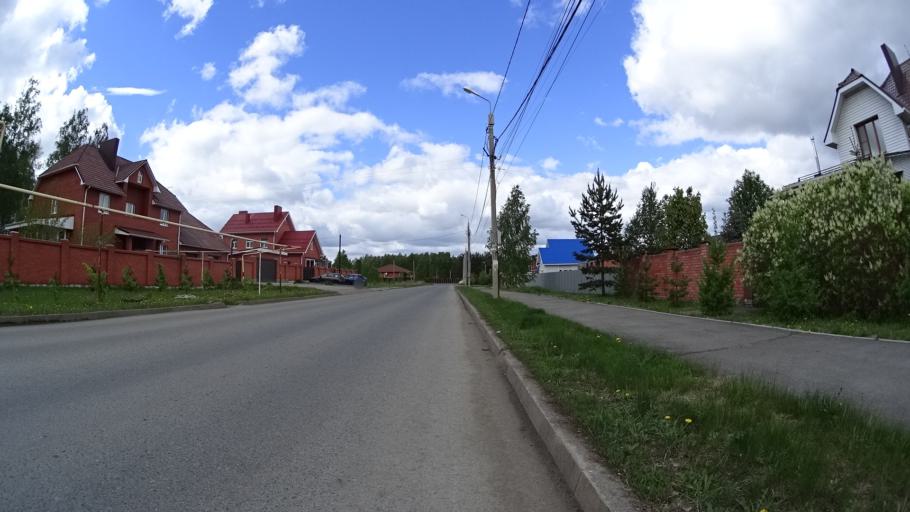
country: RU
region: Chelyabinsk
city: Sargazy
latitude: 55.1597
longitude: 61.2519
